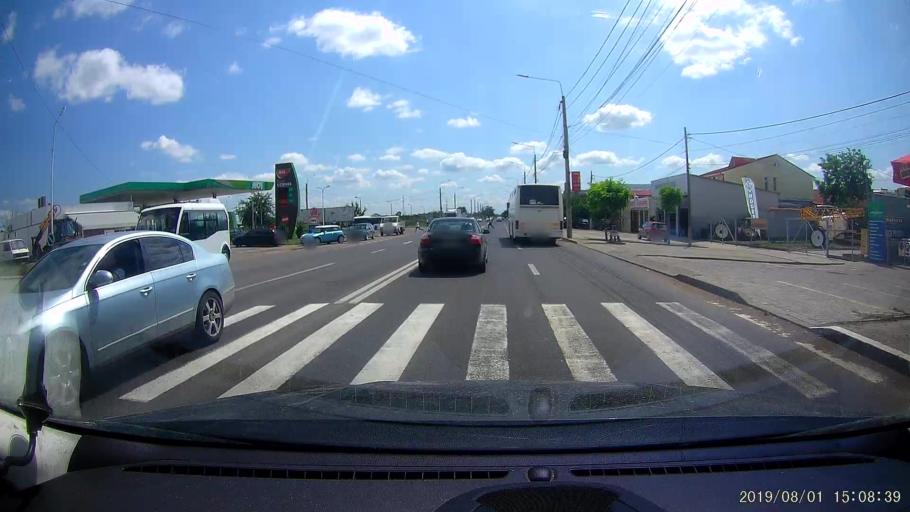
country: RO
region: Braila
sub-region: Municipiul Braila
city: Braila
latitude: 45.2397
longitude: 27.9439
